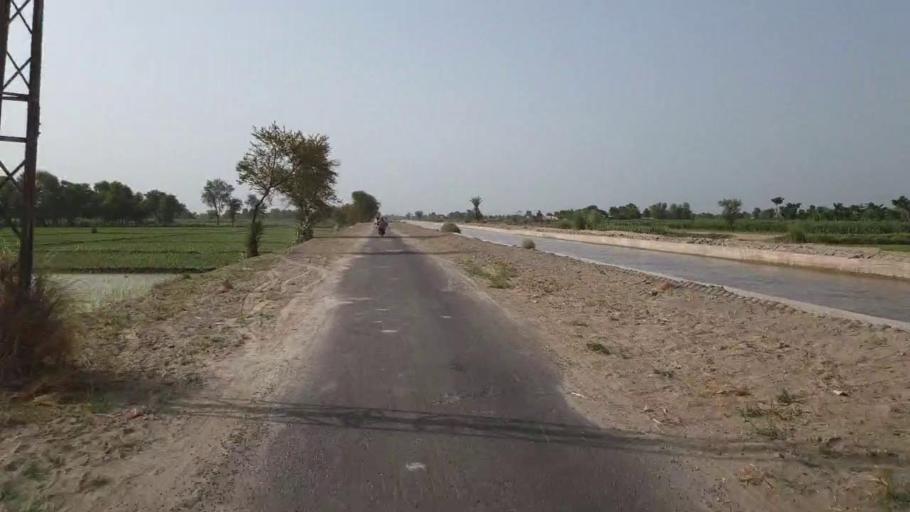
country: PK
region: Sindh
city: Daur
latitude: 26.3469
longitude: 68.1619
